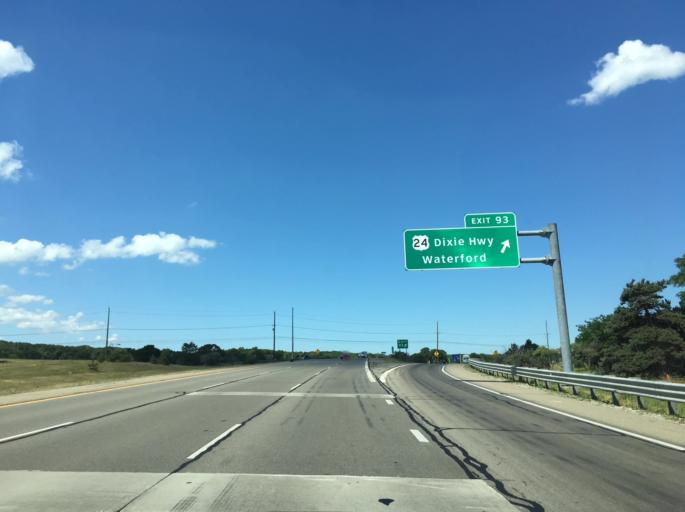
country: US
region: Michigan
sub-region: Oakland County
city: Clarkston
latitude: 42.7410
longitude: -83.4501
